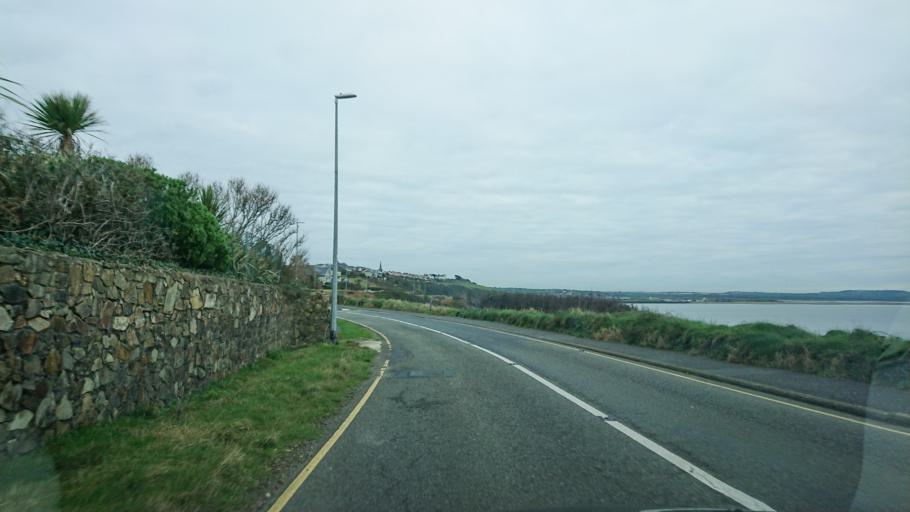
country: IE
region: Munster
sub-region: Waterford
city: Tra Mhor
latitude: 52.1498
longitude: -7.1627
